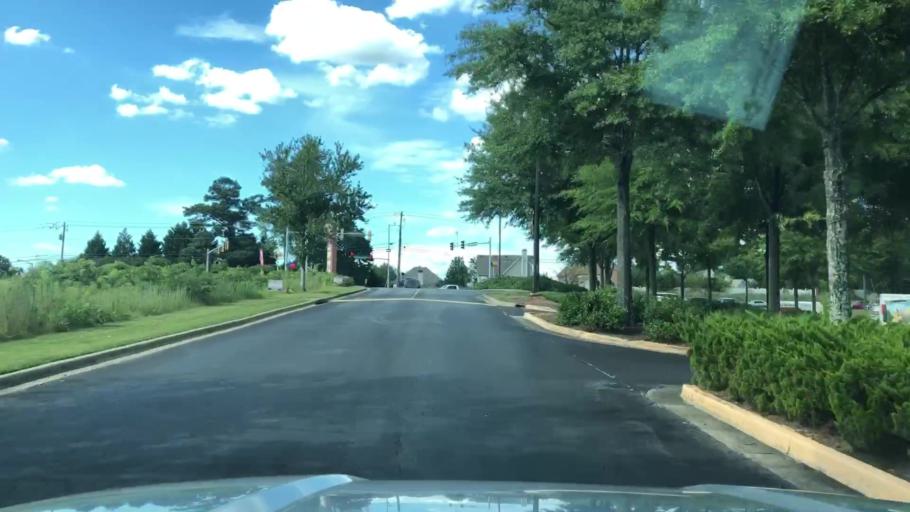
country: US
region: Georgia
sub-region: Cobb County
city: Marietta
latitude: 34.0194
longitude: -84.5258
